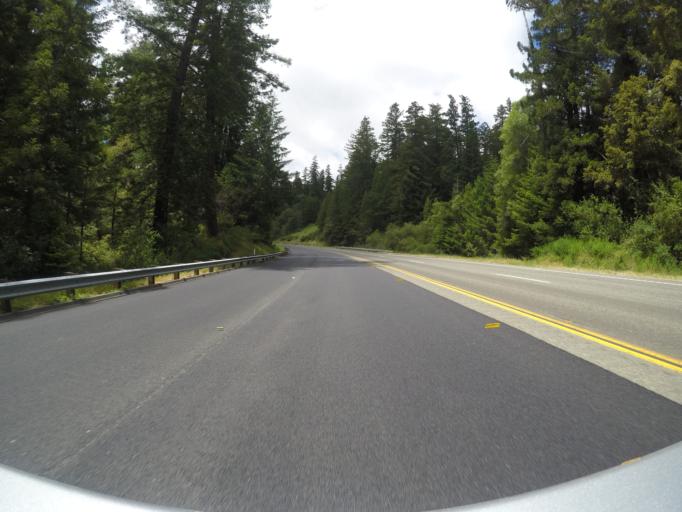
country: US
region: California
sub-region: Humboldt County
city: Redway
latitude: 40.3039
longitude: -123.8940
